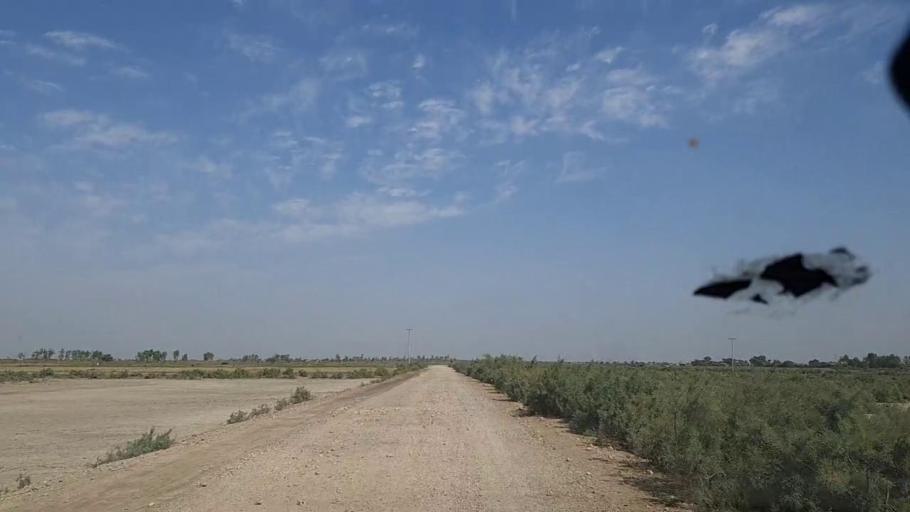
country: PK
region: Sindh
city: Daro Mehar
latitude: 24.6652
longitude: 68.0789
